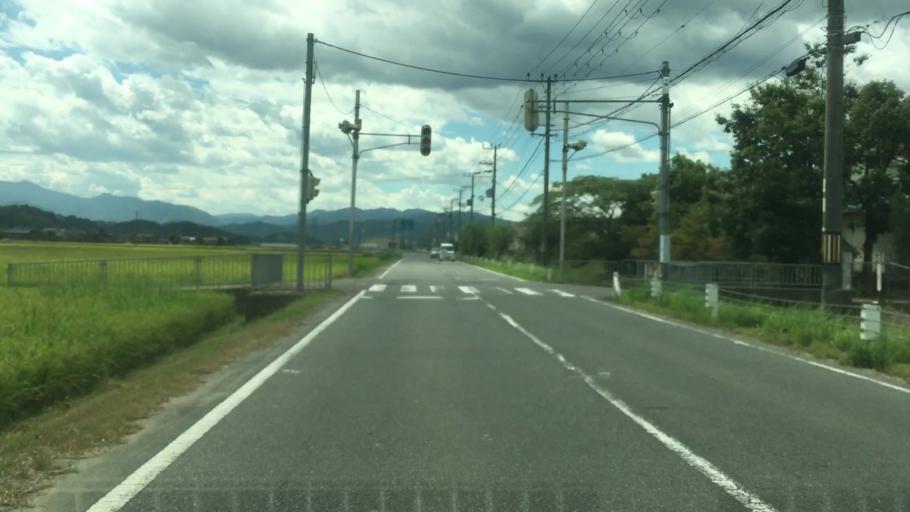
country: JP
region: Hyogo
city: Toyooka
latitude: 35.5301
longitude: 134.8398
